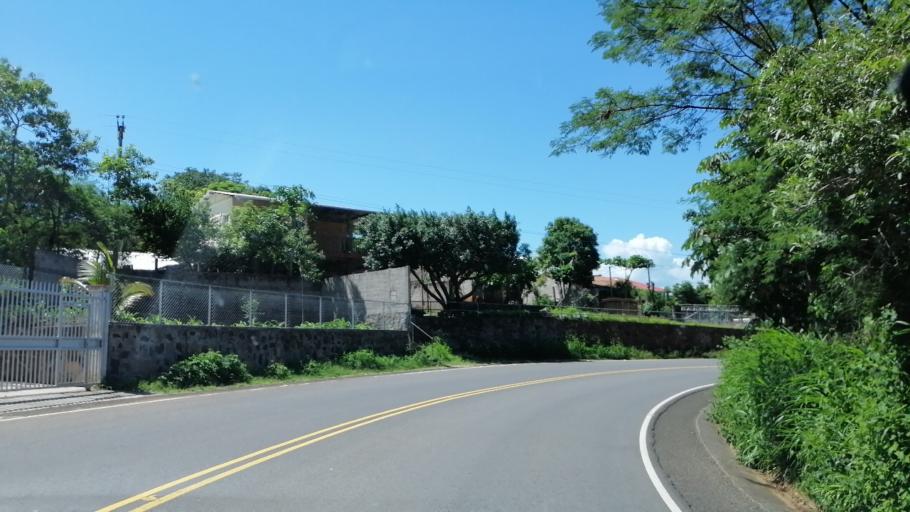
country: SV
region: San Miguel
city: Ciudad Barrios
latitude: 13.8134
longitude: -88.1763
